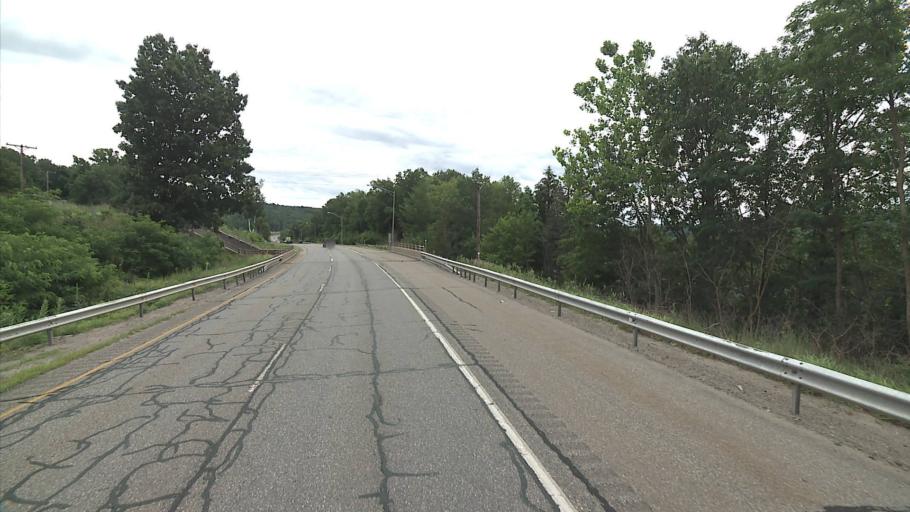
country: US
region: Connecticut
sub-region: Litchfield County
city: Torrington
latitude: 41.7986
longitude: -73.1132
